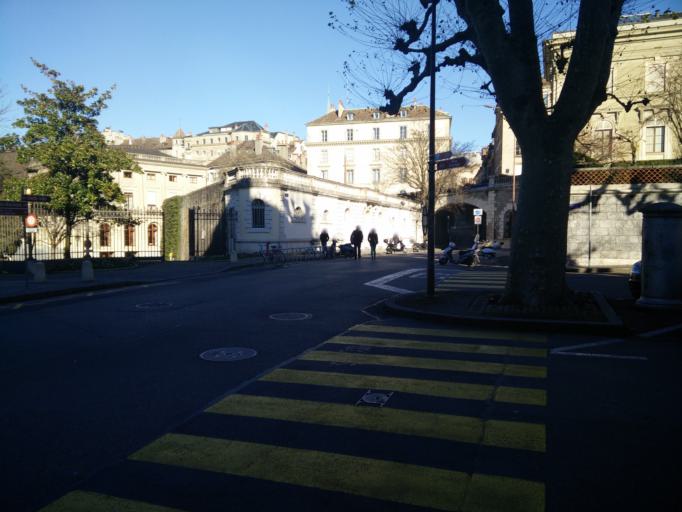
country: CH
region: Geneva
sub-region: Geneva
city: Geneve
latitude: 46.1984
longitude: 6.1471
